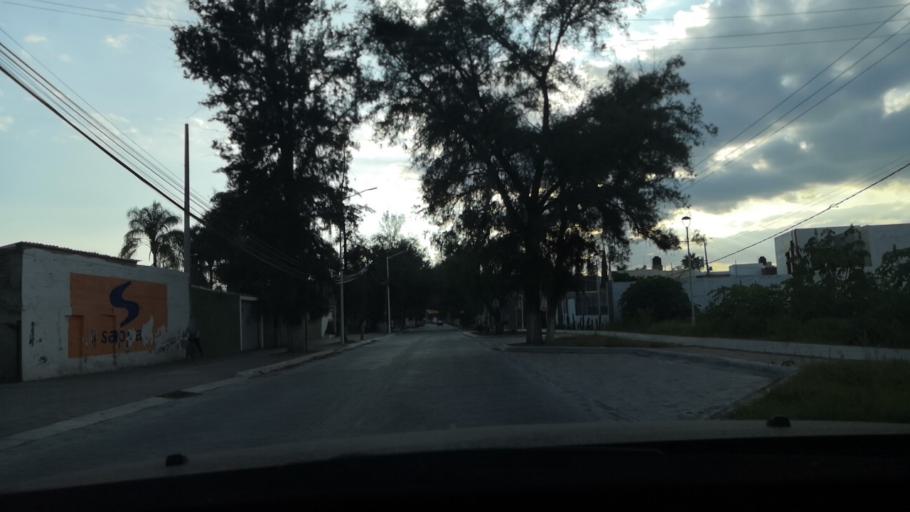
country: MX
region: Guanajuato
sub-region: San Francisco del Rincon
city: Fraccionamiento la Mezquitera
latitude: 21.0257
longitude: -101.8370
